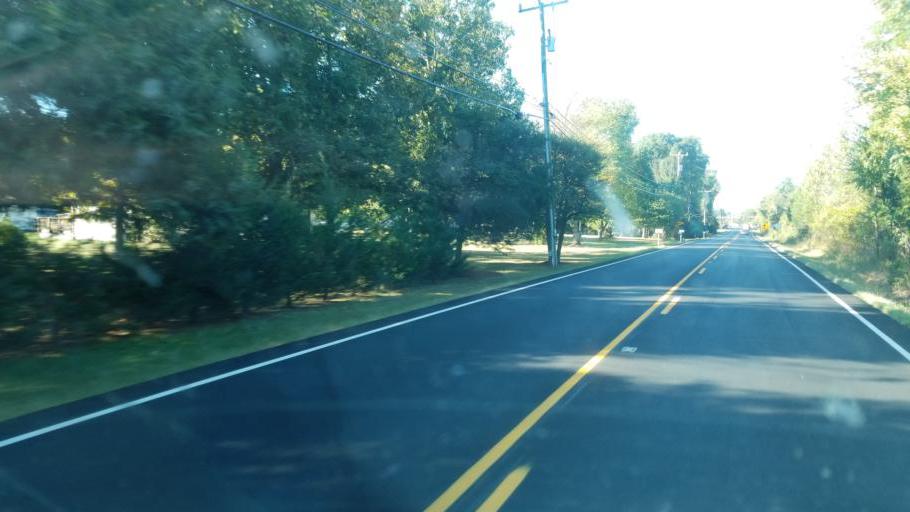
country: US
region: Virginia
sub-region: Fauquier County
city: Bealeton
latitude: 38.5653
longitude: -77.7975
